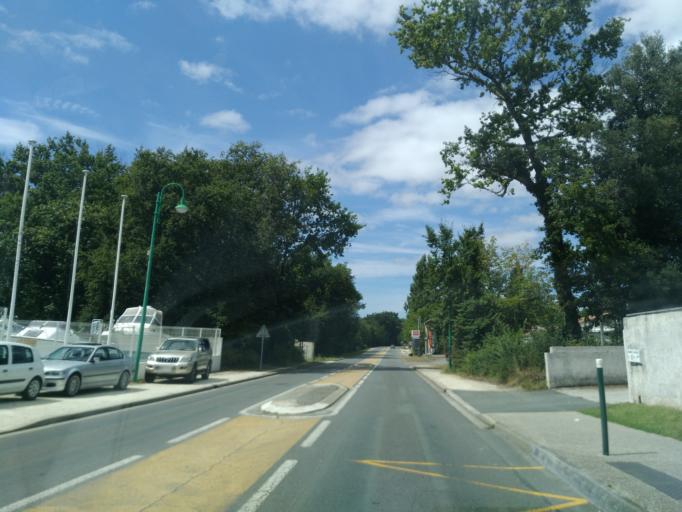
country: FR
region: Poitou-Charentes
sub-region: Departement de la Charente-Maritime
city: Breuillet
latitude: 45.6985
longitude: -1.0523
